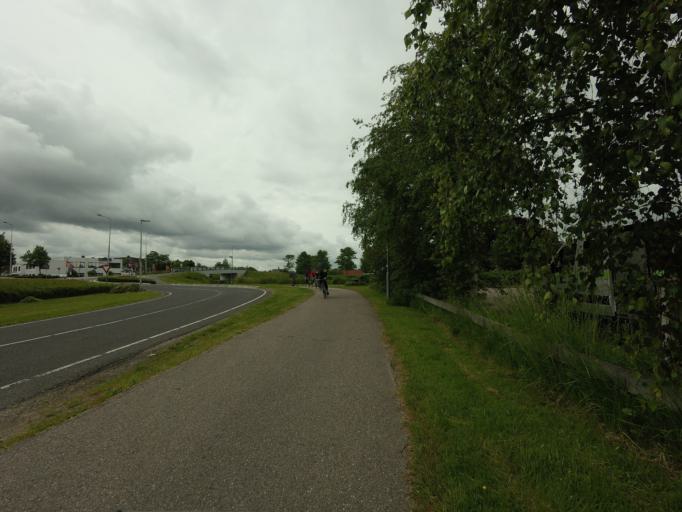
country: NL
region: North Holland
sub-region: Gemeente Purmerend
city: Purmerend
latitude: 52.5761
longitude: 4.9976
